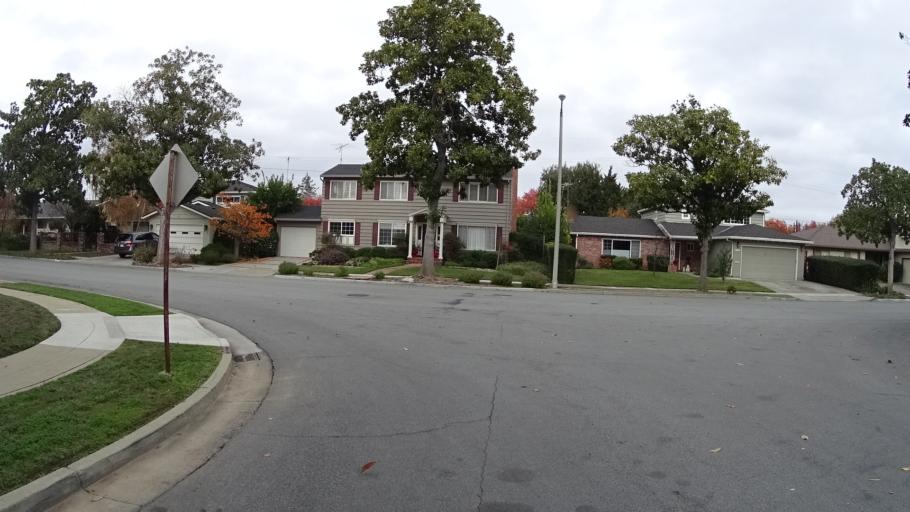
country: US
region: California
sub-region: Santa Clara County
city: Sunnyvale
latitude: 37.3609
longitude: -122.0457
